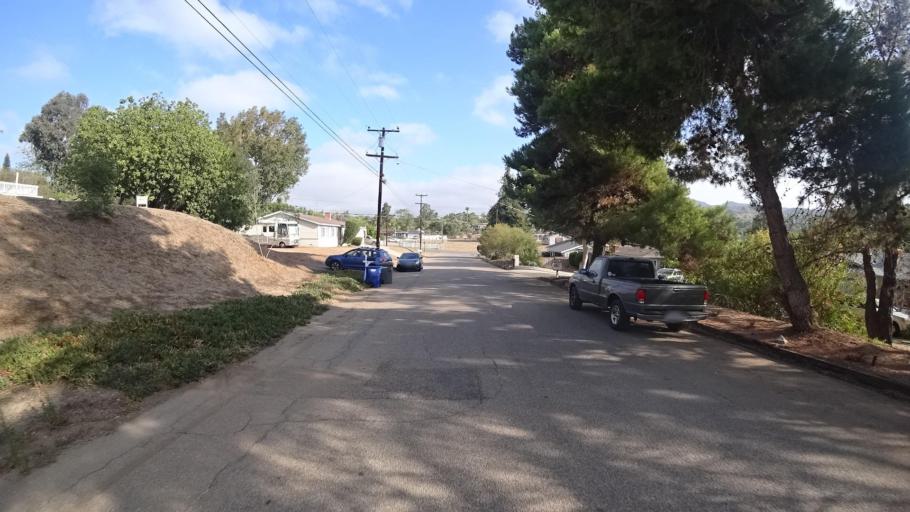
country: US
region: California
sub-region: San Diego County
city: Vista
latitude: 33.1894
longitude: -117.2030
